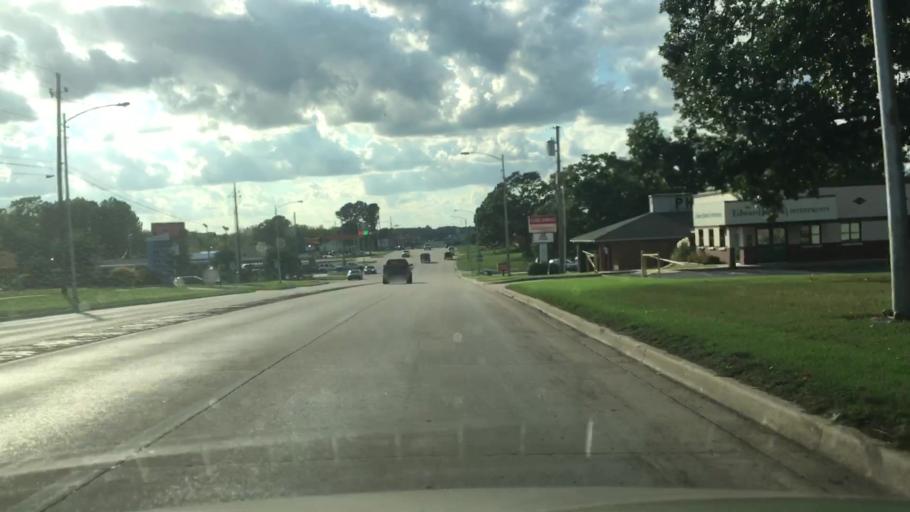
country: US
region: Oklahoma
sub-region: Cherokee County
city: Tahlequah
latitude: 35.9154
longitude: -94.9512
